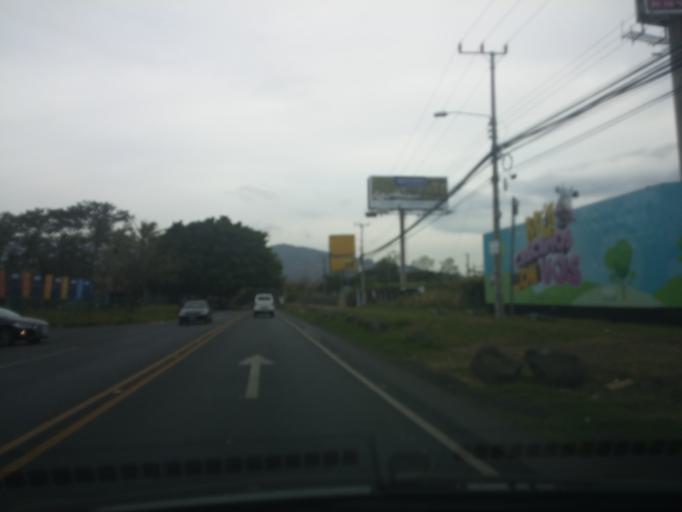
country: CR
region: Heredia
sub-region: Canton de Belen
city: San Antonio
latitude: 9.9744
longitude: -84.2000
